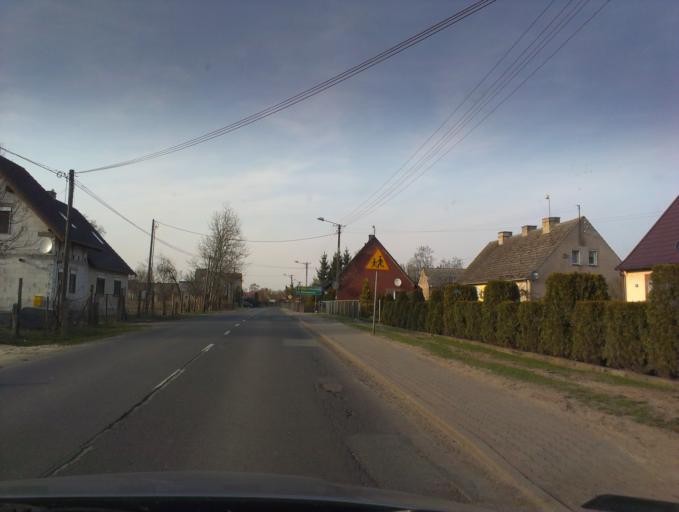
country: PL
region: Pomeranian Voivodeship
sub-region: Powiat czluchowski
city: Debrzno
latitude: 53.5234
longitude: 17.2316
